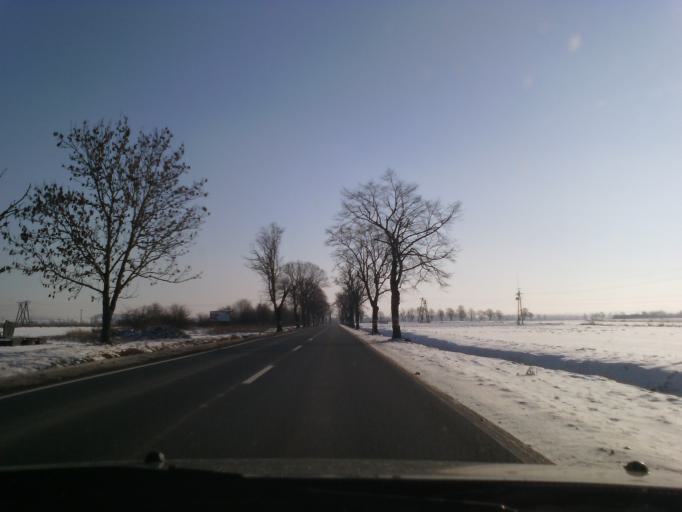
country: PL
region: Lower Silesian Voivodeship
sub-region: Powiat swidnicki
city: Stanowice
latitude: 50.9460
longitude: 16.3643
